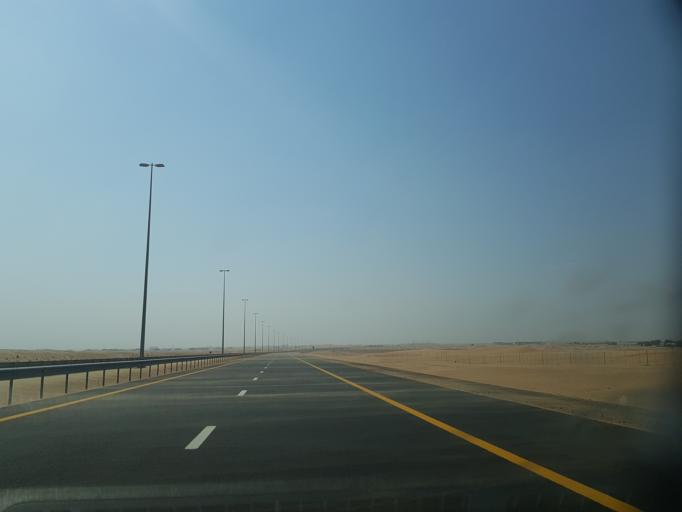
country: AE
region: Ash Shariqah
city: Sharjah
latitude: 25.2708
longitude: 55.6401
